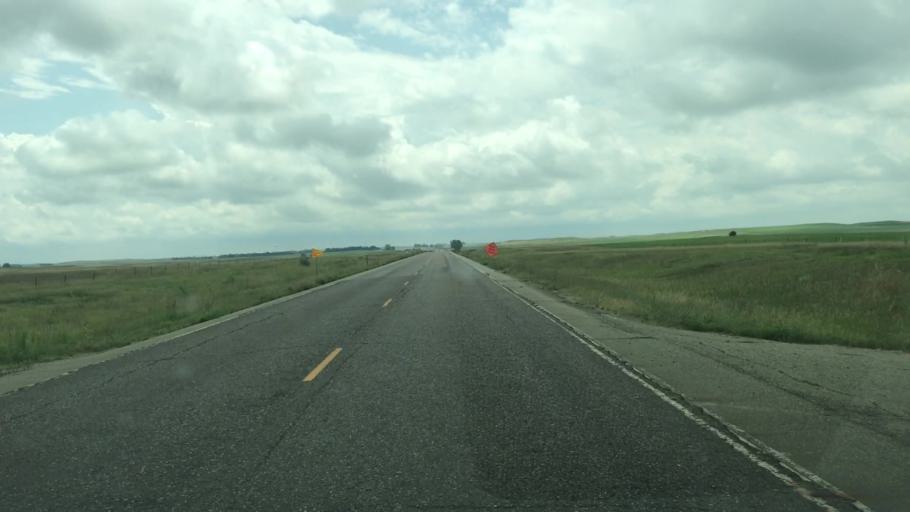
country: US
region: Nebraska
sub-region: Cherry County
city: Valentine
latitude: 43.0603
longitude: -100.5951
